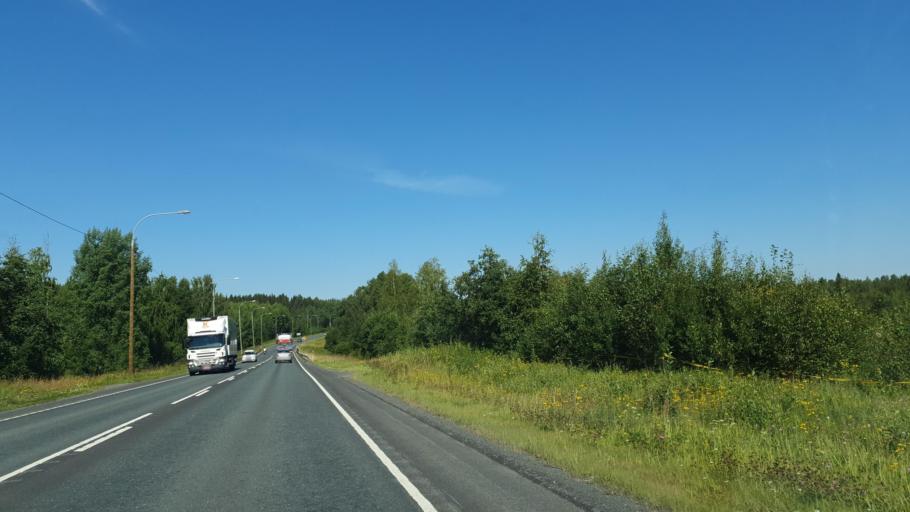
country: FI
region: Northern Savo
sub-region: Ylae-Savo
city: Lapinlahti
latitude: 63.2186
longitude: 27.5169
